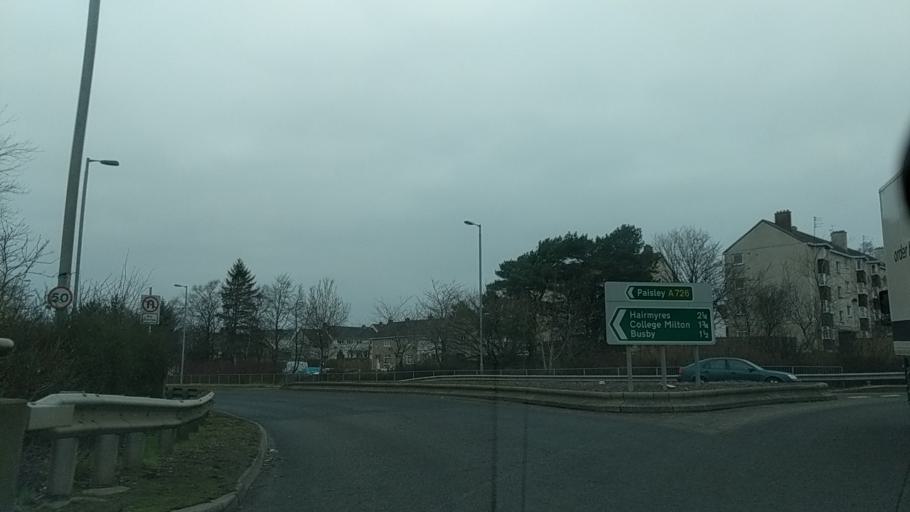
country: GB
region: Scotland
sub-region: South Lanarkshire
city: East Kilbride
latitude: 55.7602
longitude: -4.1873
